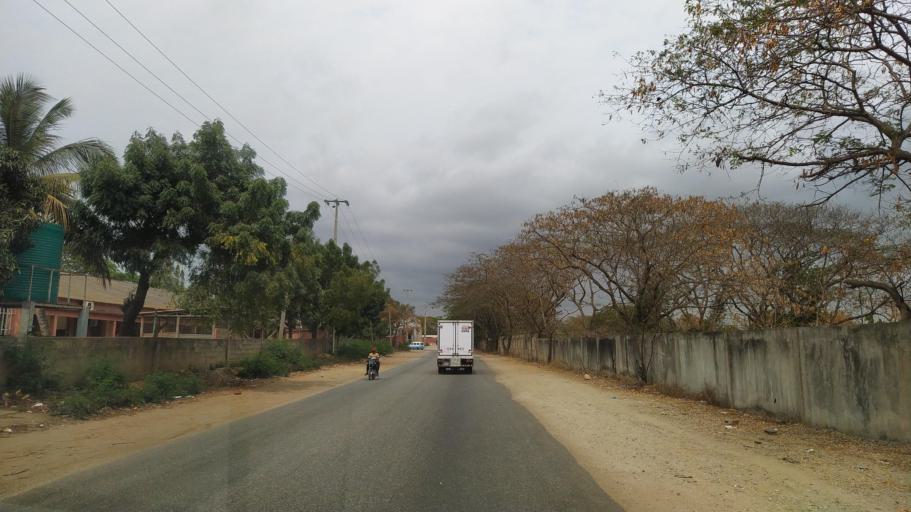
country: AO
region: Luanda
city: Luanda
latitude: -8.8576
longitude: 13.2872
